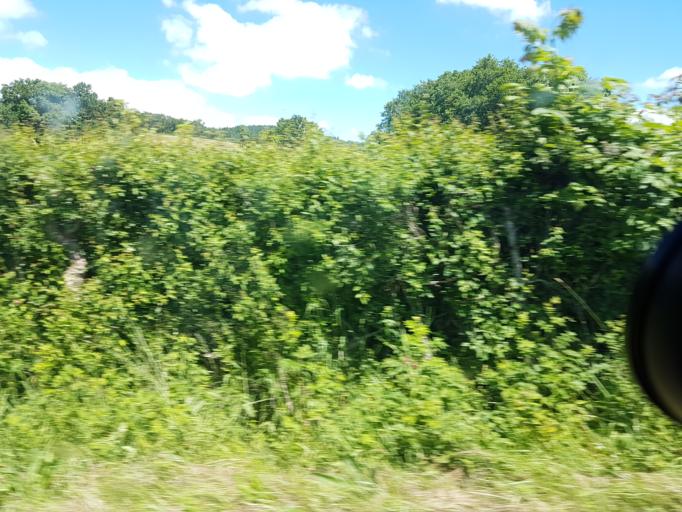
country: FR
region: Bourgogne
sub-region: Departement de Saone-et-Loire
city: Autun
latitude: 47.0582
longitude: 4.2684
